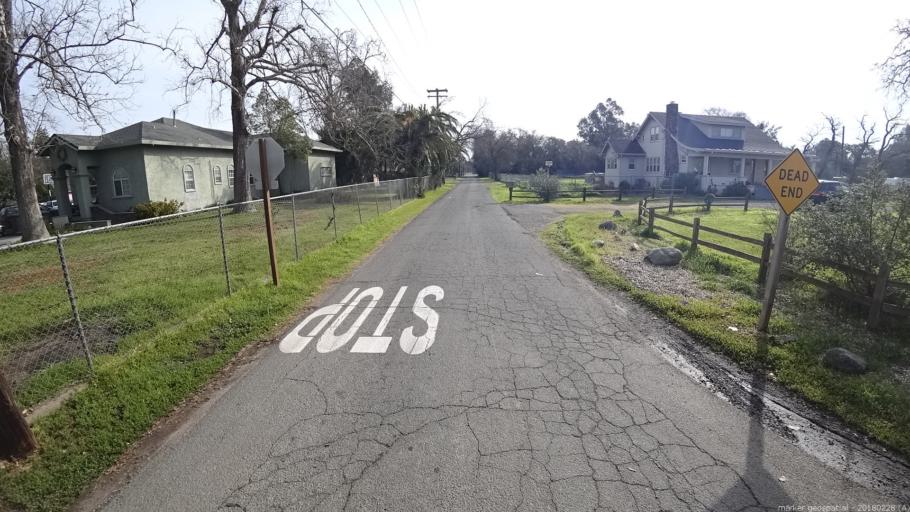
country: US
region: California
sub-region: Sacramento County
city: Rio Linda
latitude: 38.6946
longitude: -121.4382
